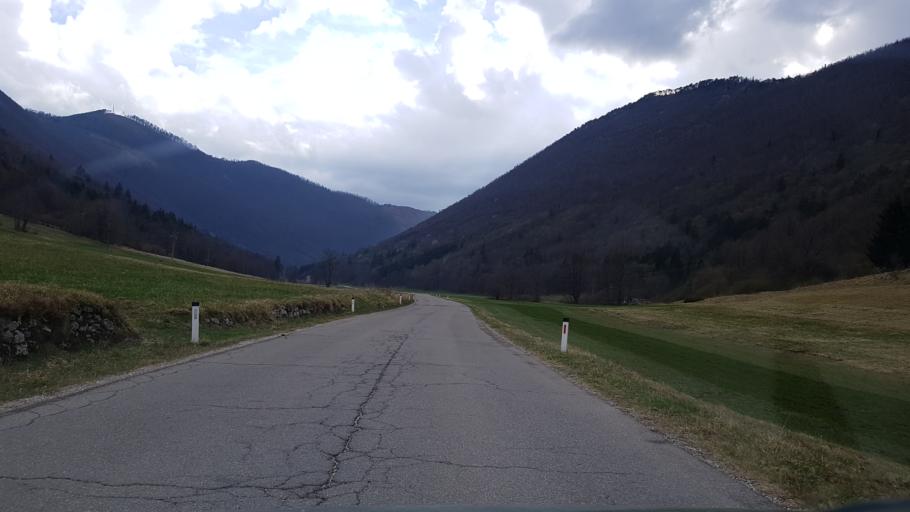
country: SI
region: Nova Gorica
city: Sempas
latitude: 46.0404
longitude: 13.7866
